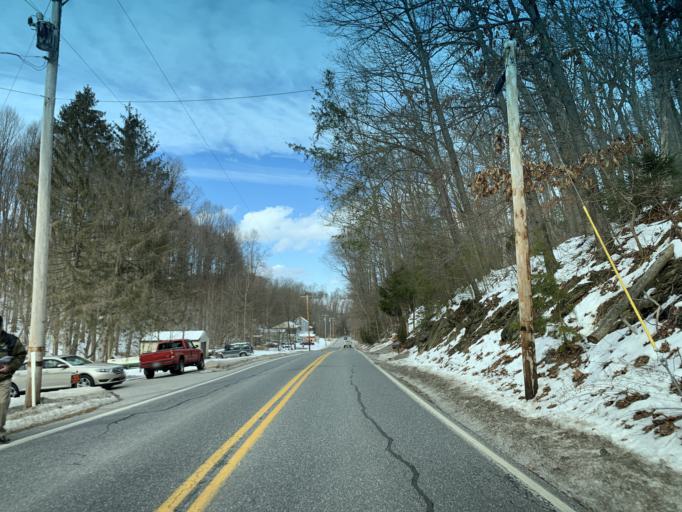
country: US
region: Pennsylvania
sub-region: York County
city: Shrewsbury
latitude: 39.8128
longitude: -76.6296
